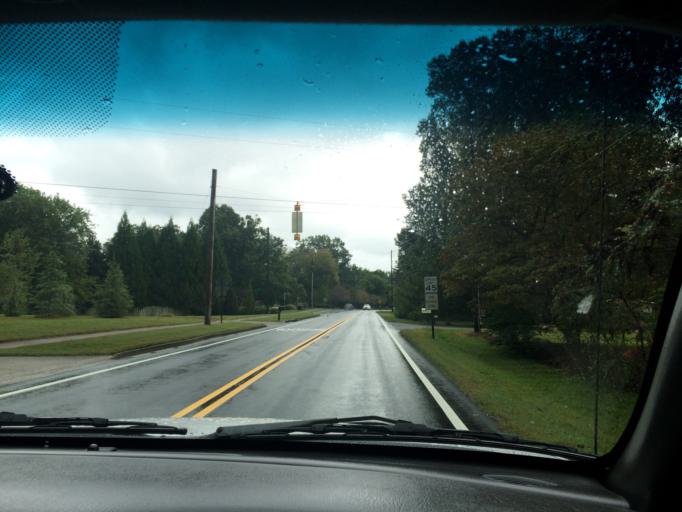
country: US
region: Georgia
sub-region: Cobb County
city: Kennesaw
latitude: 34.0365
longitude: -84.6447
